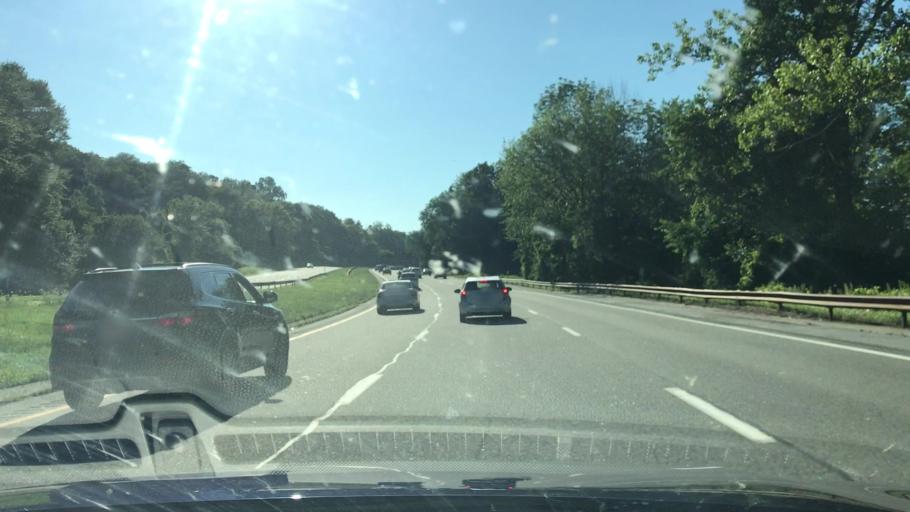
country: US
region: New York
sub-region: Westchester County
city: Yorktown Heights
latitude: 41.2753
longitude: -73.8114
